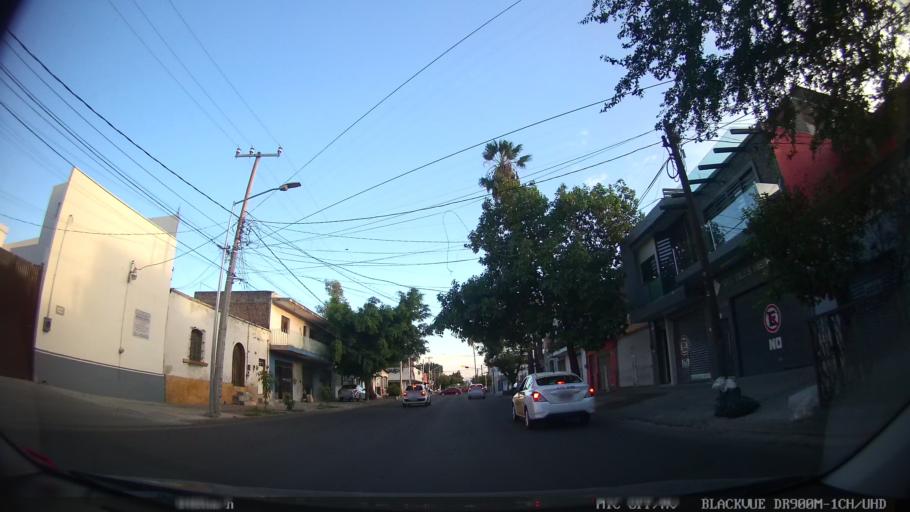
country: MX
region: Jalisco
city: Tlaquepaque
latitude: 20.6882
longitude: -103.3084
